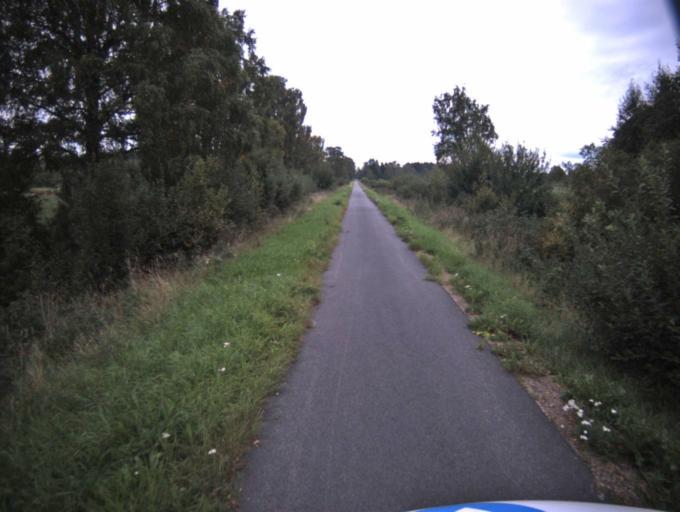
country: SE
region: Vaestra Goetaland
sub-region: Falkopings Kommun
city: Falkoeping
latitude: 58.0019
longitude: 13.5474
